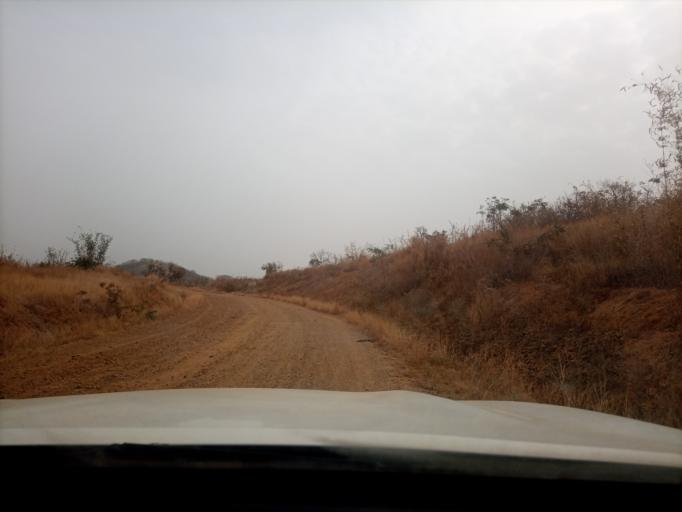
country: ET
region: Oromiya
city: Mendi
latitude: 10.1915
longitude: 35.0574
